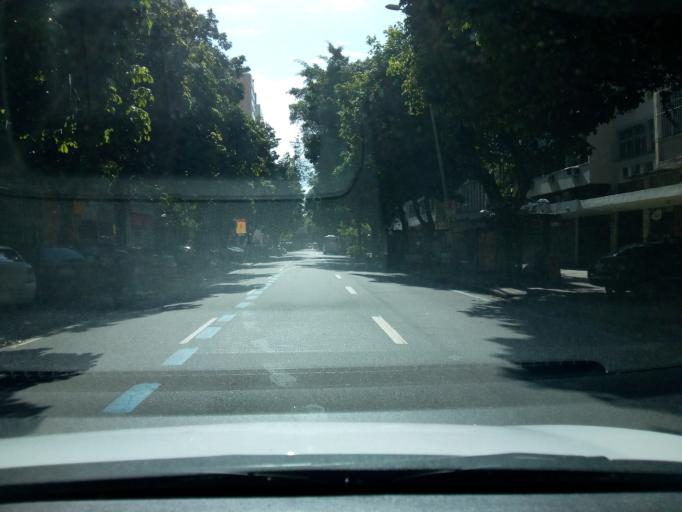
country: BR
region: Rio de Janeiro
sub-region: Rio De Janeiro
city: Rio de Janeiro
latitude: -22.9843
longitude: -43.2045
